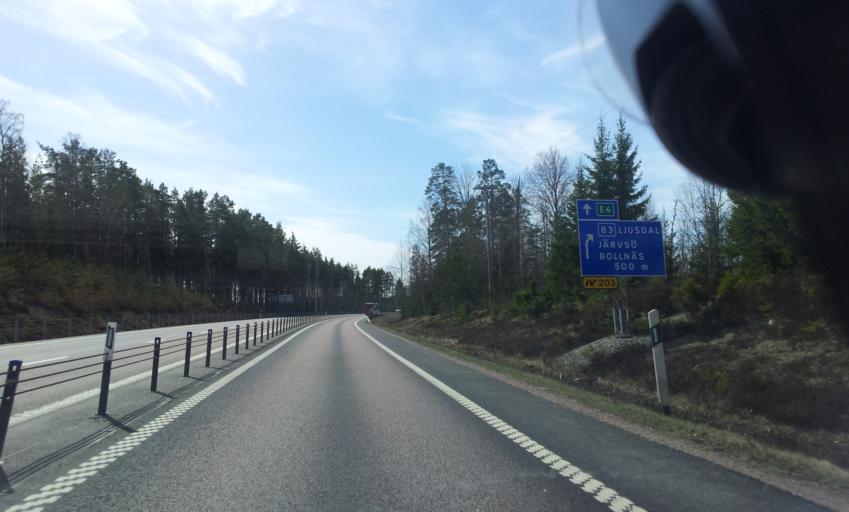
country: SE
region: Gaevleborg
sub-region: Gavle Kommun
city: Norrsundet
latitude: 61.0829
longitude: 16.9723
